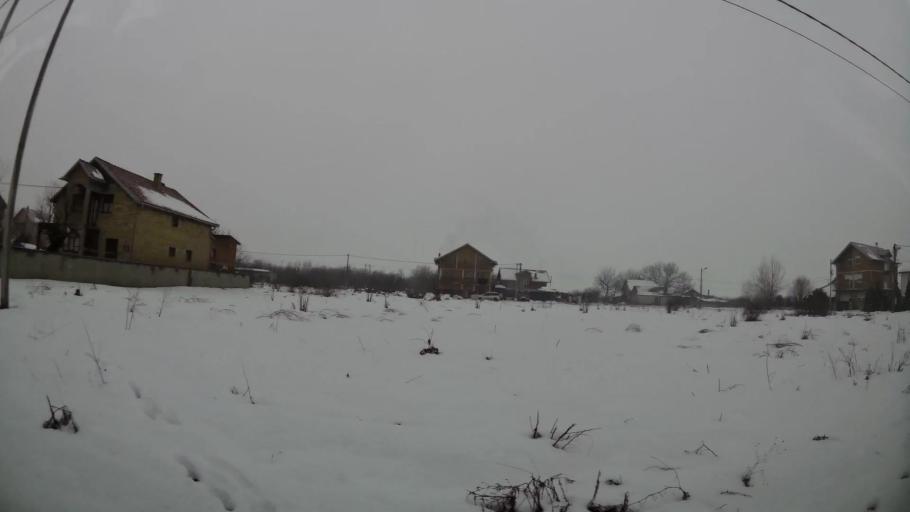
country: RS
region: Central Serbia
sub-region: Belgrade
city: Surcin
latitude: 44.8741
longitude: 20.3129
